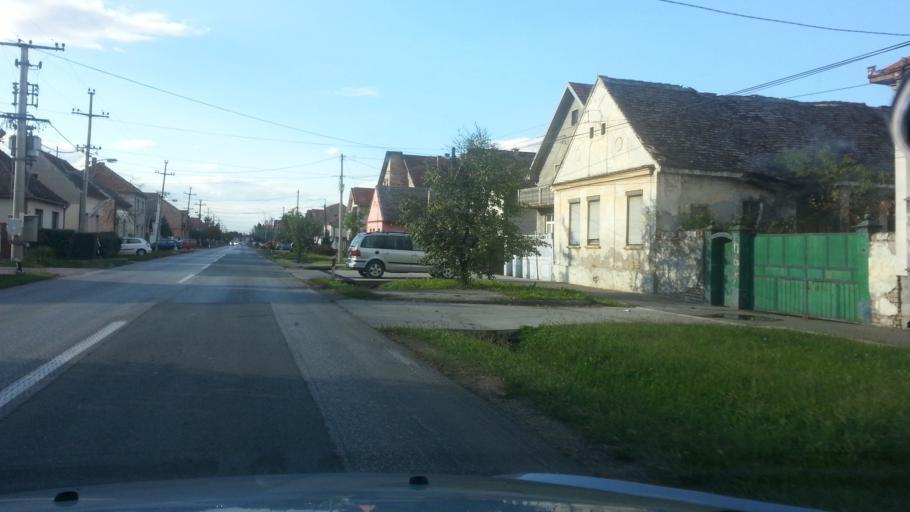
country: RS
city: Novi Banovci
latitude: 44.9090
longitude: 20.2699
